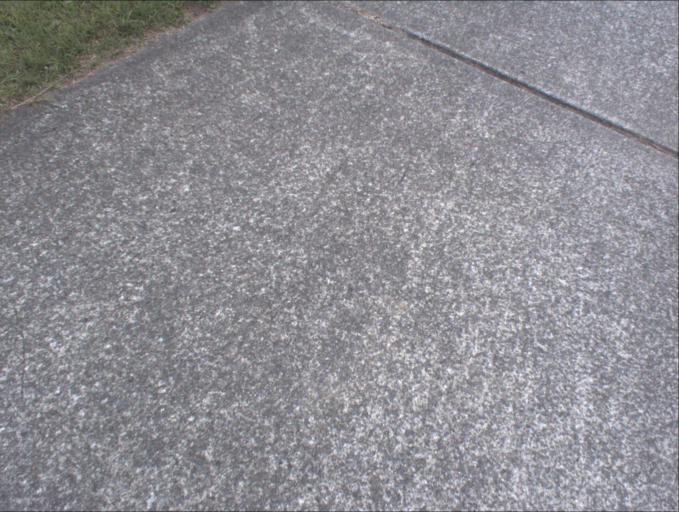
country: AU
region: Queensland
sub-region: Logan
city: Waterford West
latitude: -27.6950
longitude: 153.1539
